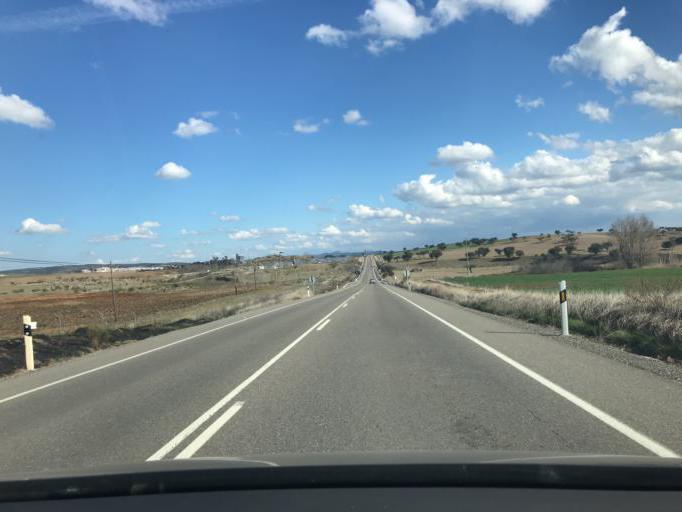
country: ES
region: Andalusia
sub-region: Province of Cordoba
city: Penarroya-Pueblonuevo
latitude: 38.2998
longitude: -5.3120
